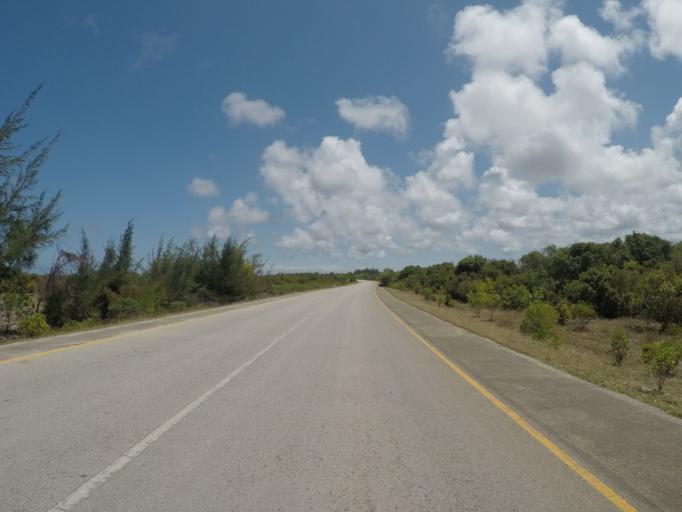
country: TZ
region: Zanzibar Central/South
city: Nganane
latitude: -6.3828
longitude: 39.5638
